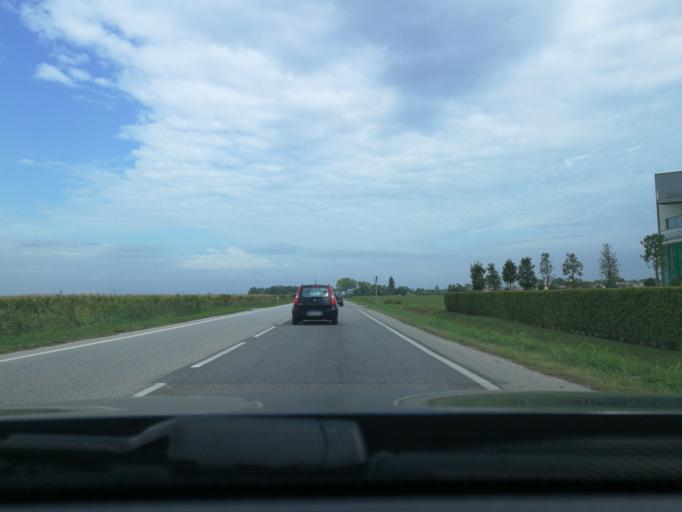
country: IT
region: Veneto
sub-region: Provincia di Venezia
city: Bibione
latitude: 45.6651
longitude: 13.0575
